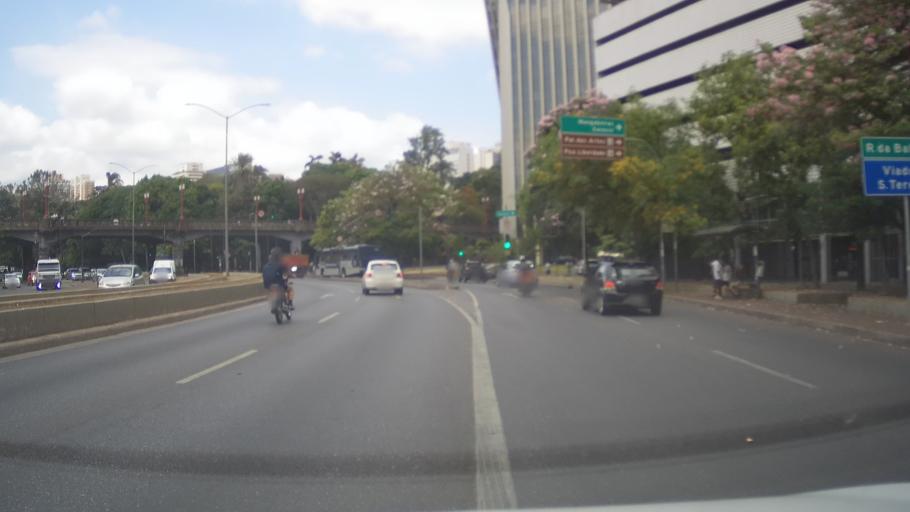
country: BR
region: Minas Gerais
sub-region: Belo Horizonte
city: Belo Horizonte
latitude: -19.9188
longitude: -43.9351
